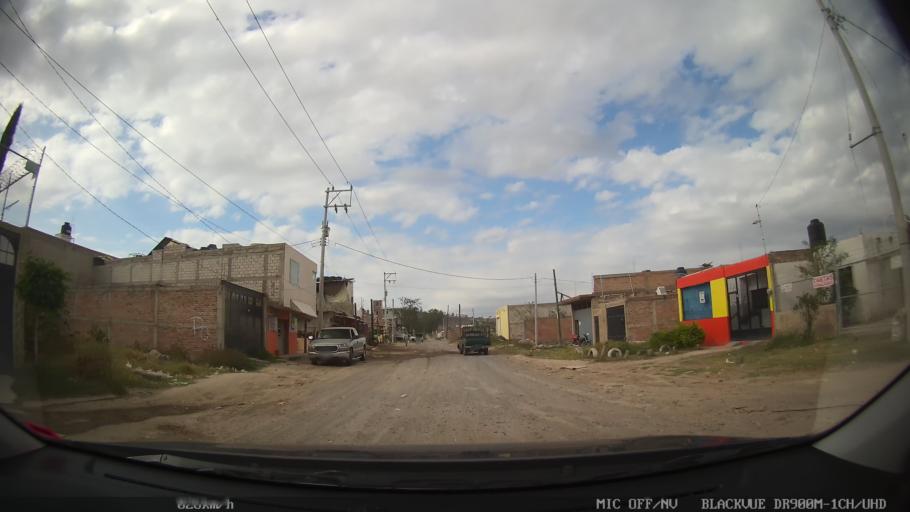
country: MX
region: Jalisco
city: Tonala
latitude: 20.6560
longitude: -103.2416
